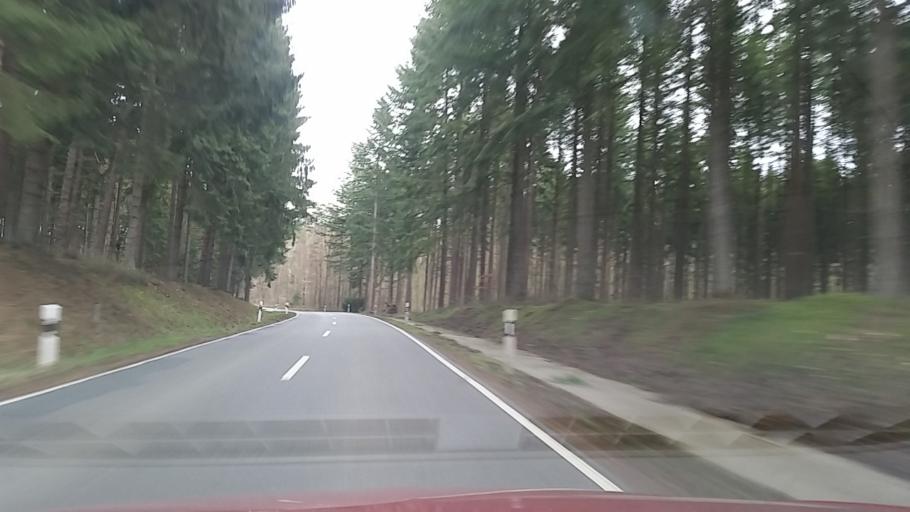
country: DE
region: Lower Saxony
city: Zernien
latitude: 53.0888
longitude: 10.9454
